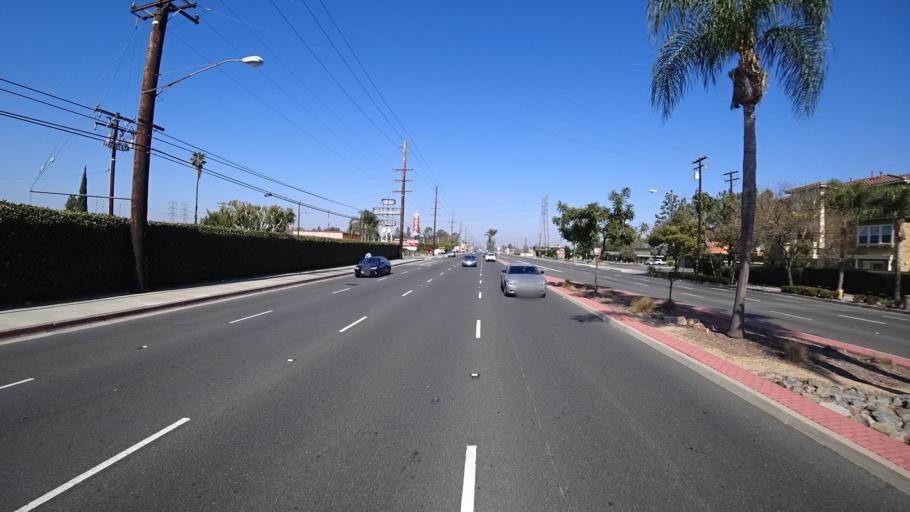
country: US
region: California
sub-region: Orange County
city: Stanton
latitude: 33.7985
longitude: -117.9931
